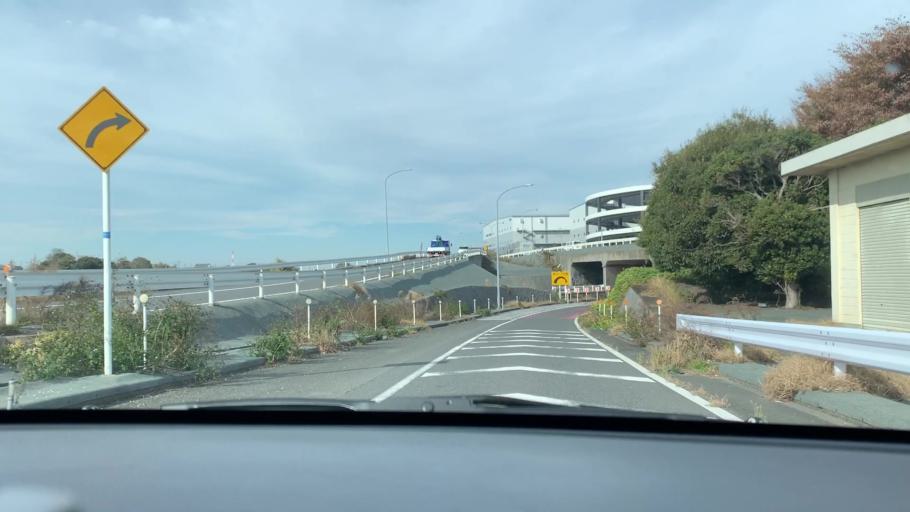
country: JP
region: Chiba
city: Nagareyama
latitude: 35.8832
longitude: 139.8977
